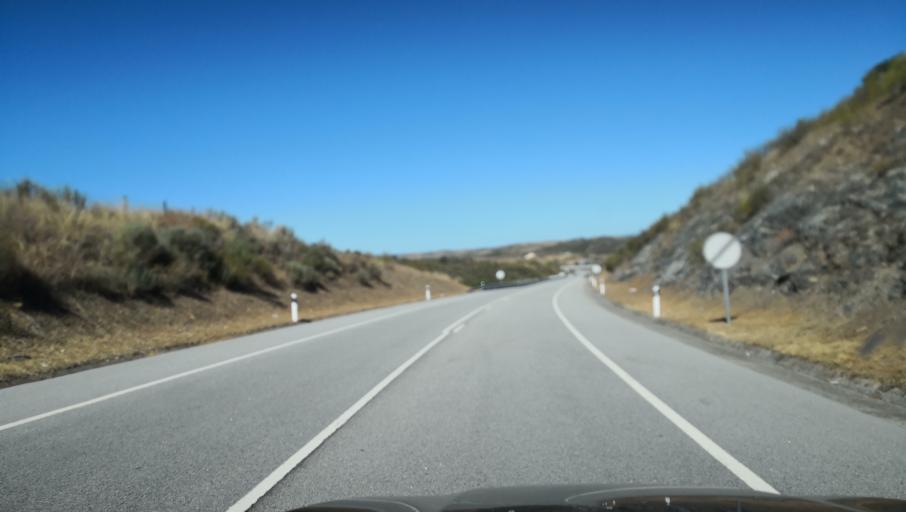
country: PT
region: Braganca
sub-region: Mirandela
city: Mirandela
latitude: 41.5025
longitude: -7.2309
